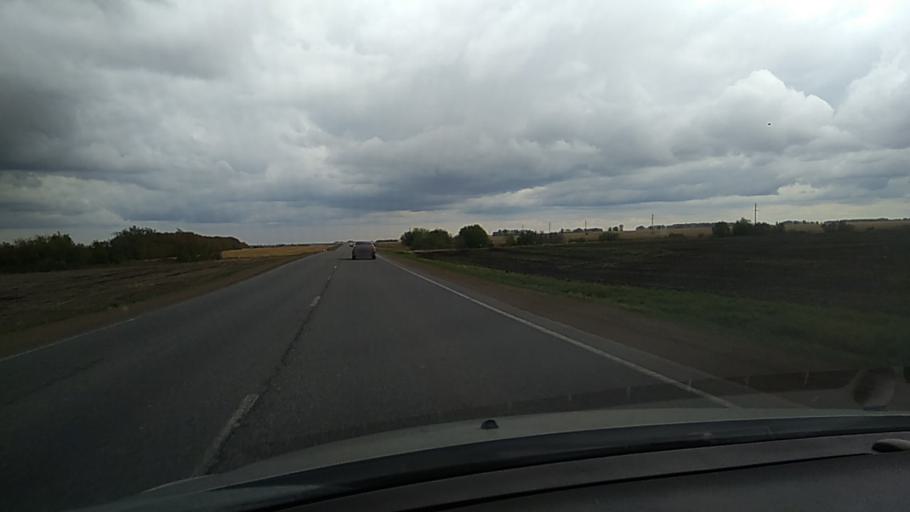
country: RU
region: Kurgan
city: Dalmatovo
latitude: 56.2896
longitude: 62.8066
